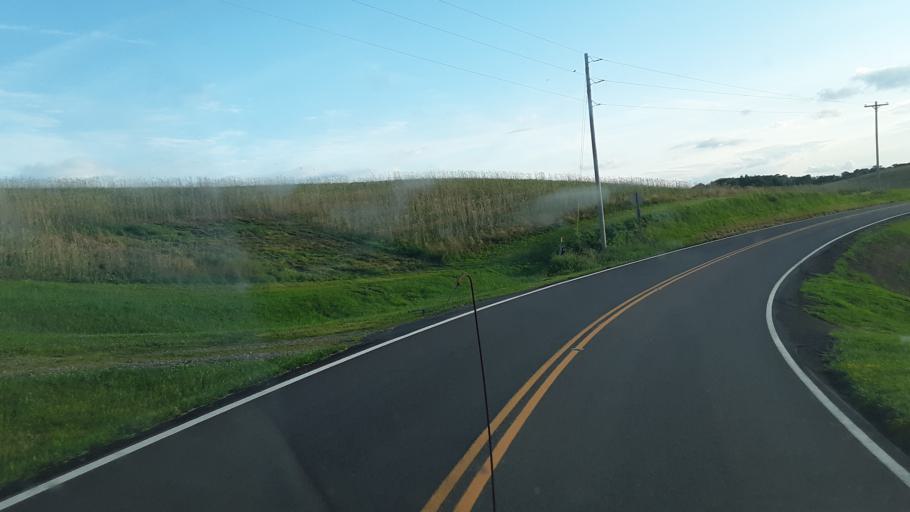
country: US
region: Ohio
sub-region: Harrison County
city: Cadiz
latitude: 40.4001
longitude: -80.9906
